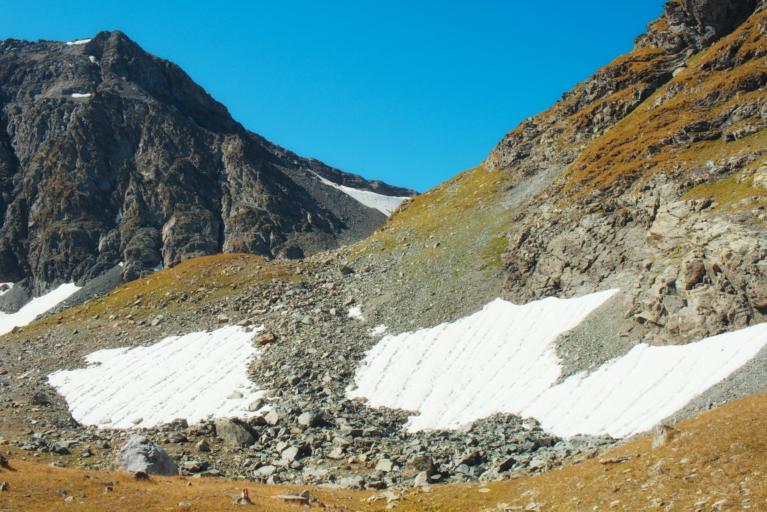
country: RU
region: Karachayevo-Cherkesiya
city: Nizhniy Arkhyz
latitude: 43.5944
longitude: 41.1914
